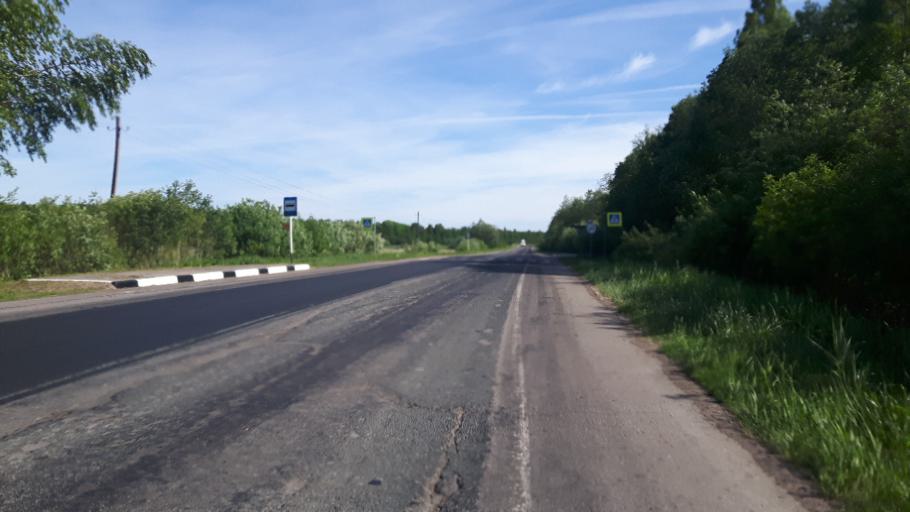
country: RU
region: Leningrad
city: Ivangorod
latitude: 59.4152
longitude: 28.3813
